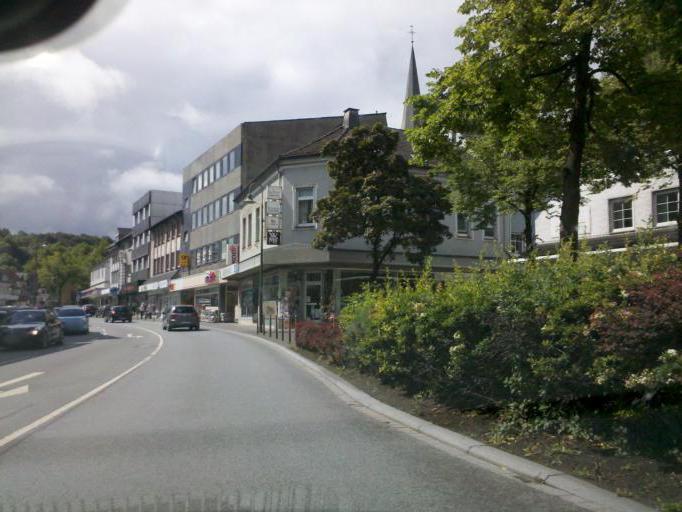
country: DE
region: North Rhine-Westphalia
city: Warstein
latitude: 51.4442
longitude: 8.3539
